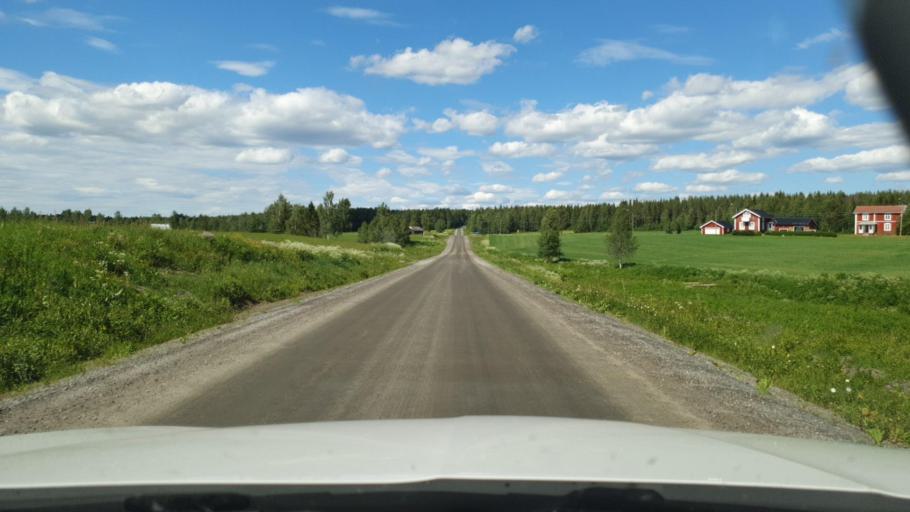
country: SE
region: Vaesterbotten
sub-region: Skelleftea Kommun
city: Forsbacka
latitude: 64.7869
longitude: 20.5117
